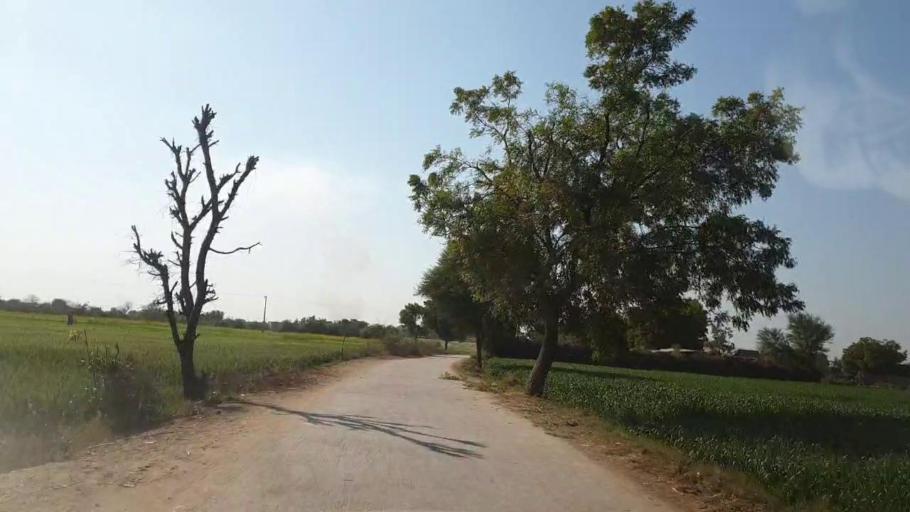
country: PK
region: Sindh
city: Tando Allahyar
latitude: 25.4825
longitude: 68.6806
